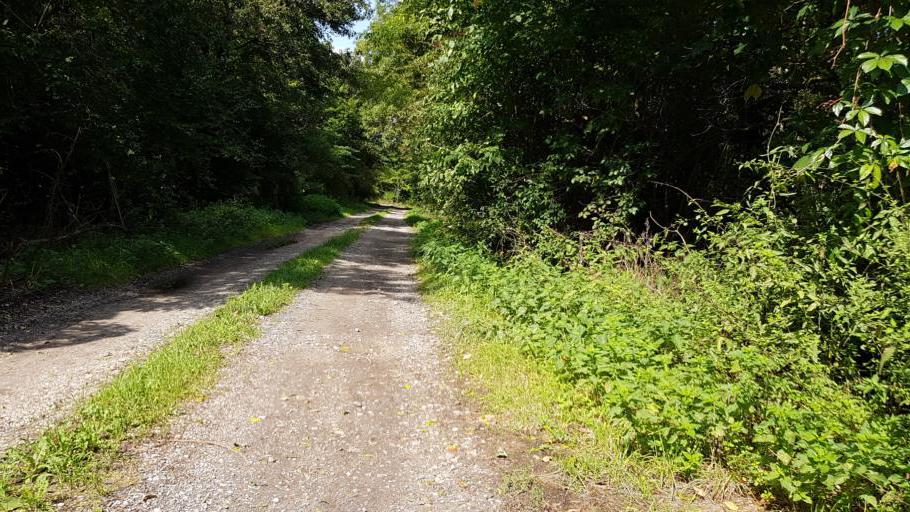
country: DE
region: Bavaria
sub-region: Upper Bavaria
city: Karlsfeld
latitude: 48.2139
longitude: 11.5042
